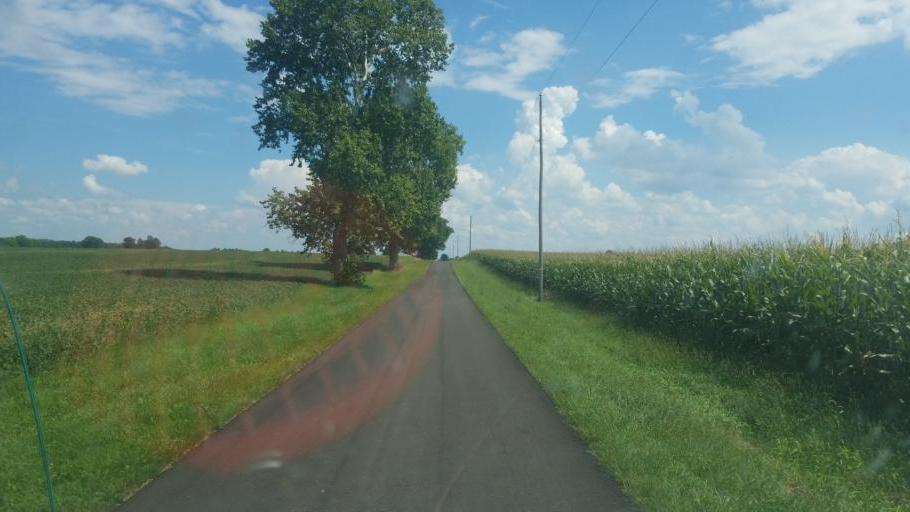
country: US
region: Ohio
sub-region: Hardin County
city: Forest
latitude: 40.8470
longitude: -83.4459
